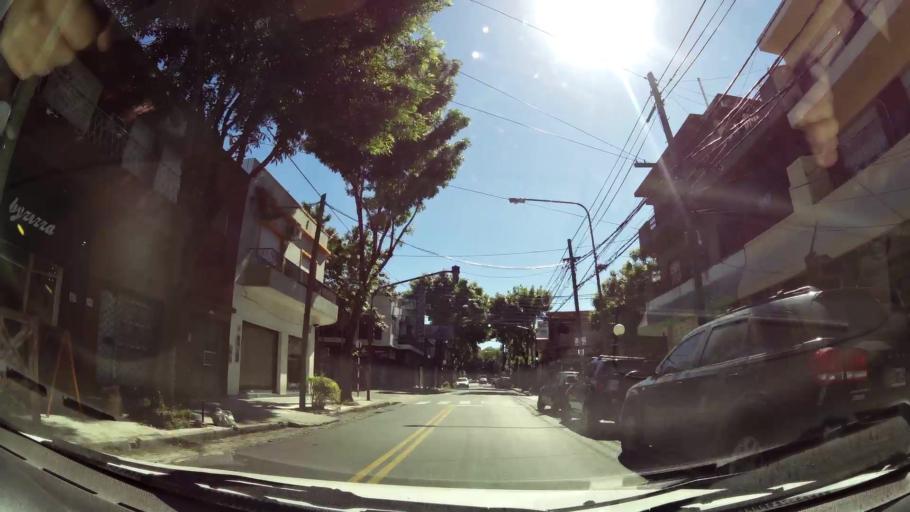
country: AR
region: Buenos Aires
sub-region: Partido de Vicente Lopez
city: Olivos
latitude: -34.5268
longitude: -58.5173
